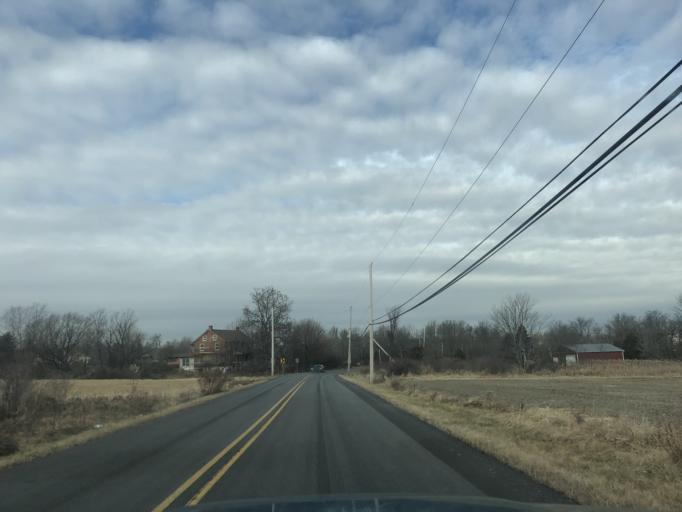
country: US
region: Pennsylvania
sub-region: Bucks County
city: Spinnerstown
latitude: 40.4419
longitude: -75.4159
